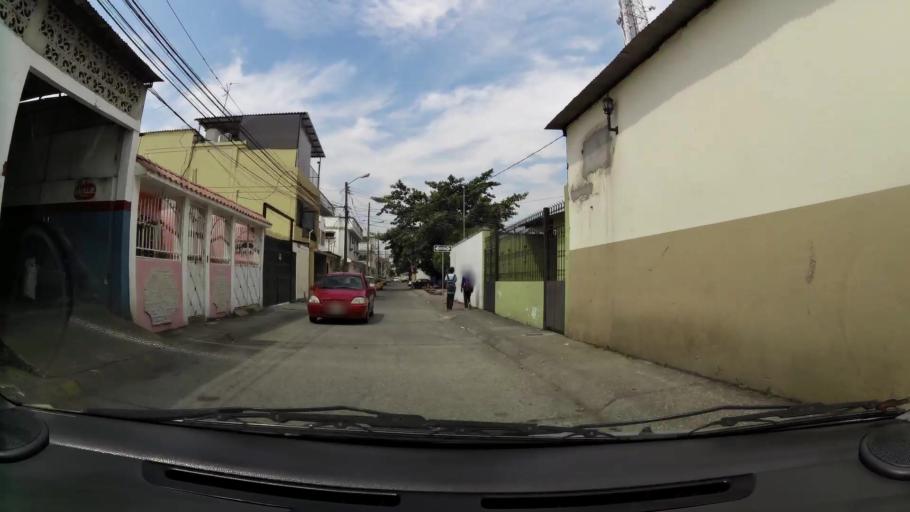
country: EC
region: Guayas
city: Eloy Alfaro
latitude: -2.1227
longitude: -79.9000
